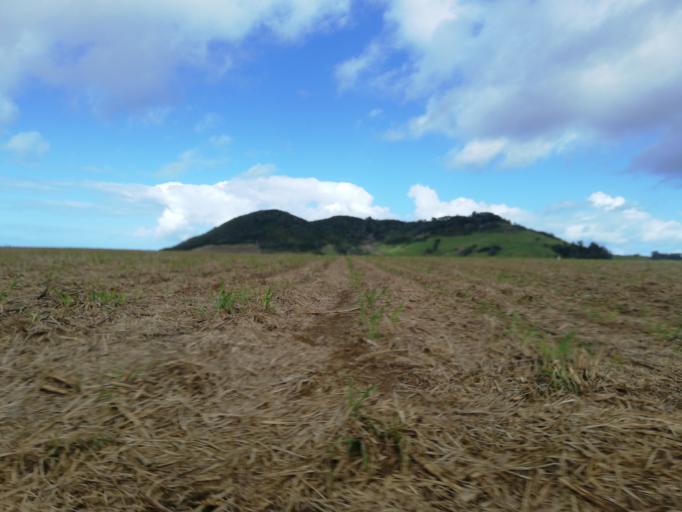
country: MU
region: Flacq
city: Grande Riviere Sud Est
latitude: -20.2813
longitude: 57.7571
